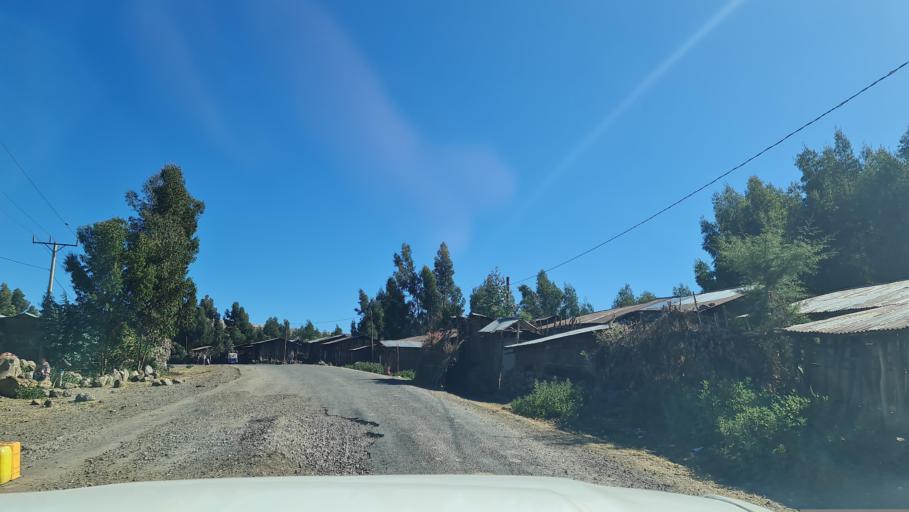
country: ET
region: Amhara
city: Debark'
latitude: 13.0983
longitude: 38.1415
